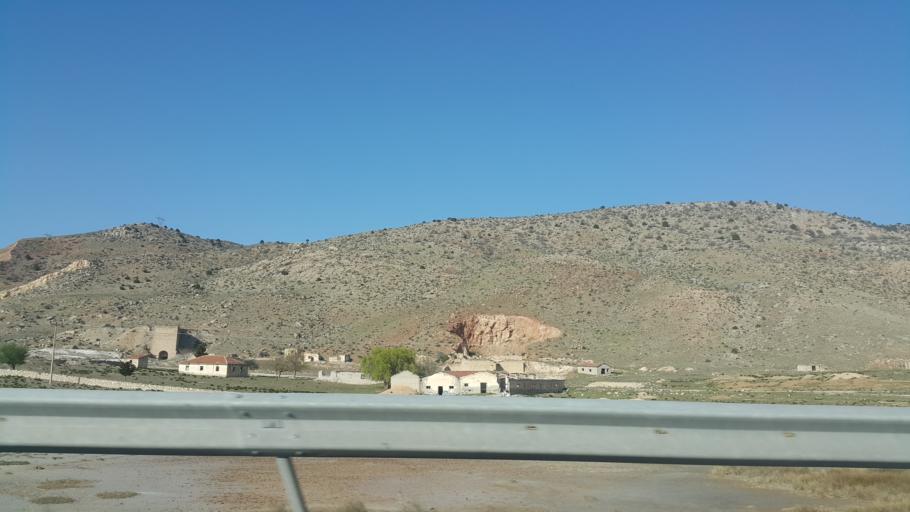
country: TR
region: Ankara
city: Sereflikochisar
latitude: 38.7707
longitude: 33.6502
